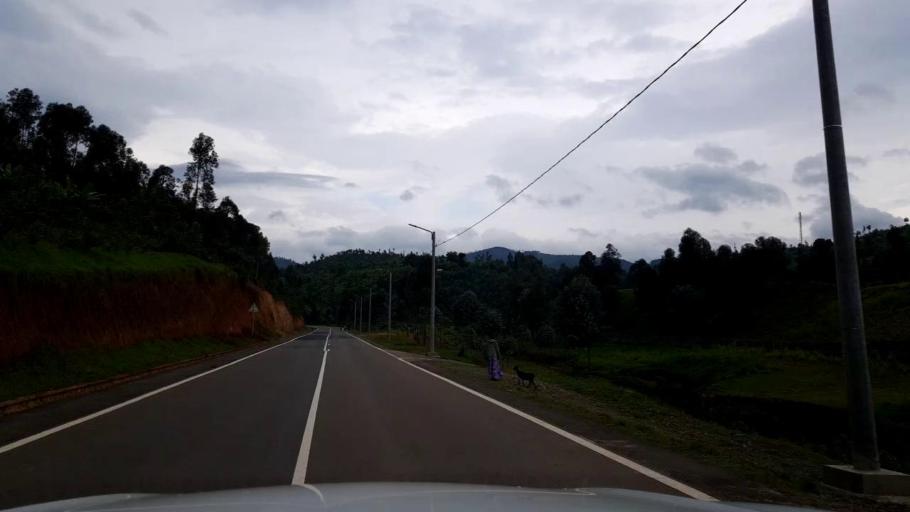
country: RW
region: Western Province
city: Kibuye
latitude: -2.0197
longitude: 29.3909
